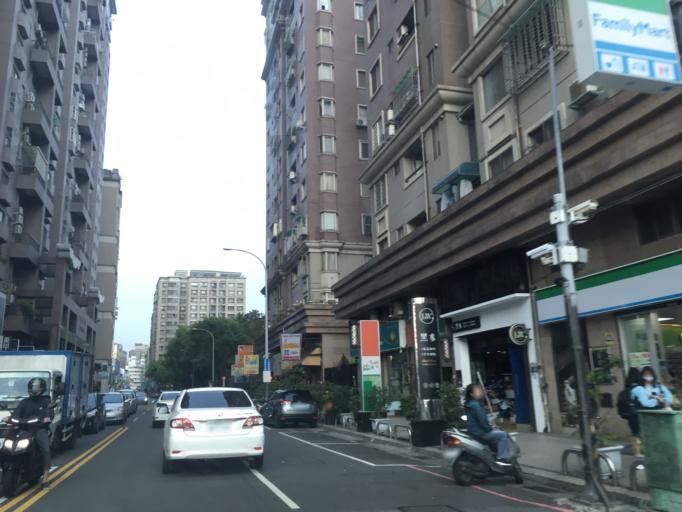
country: TW
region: Taiwan
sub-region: Taichung City
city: Taichung
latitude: 24.1758
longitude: 120.6858
